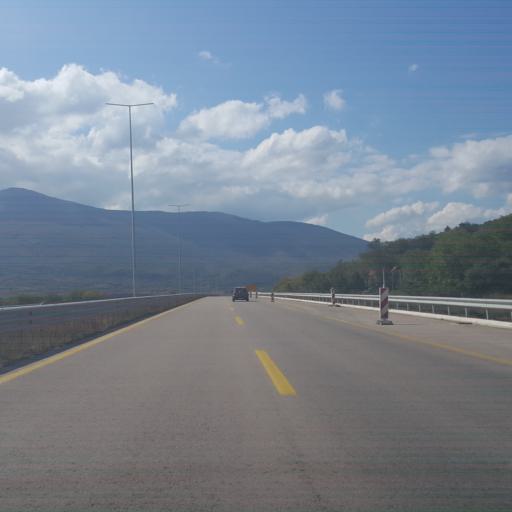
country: RS
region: Central Serbia
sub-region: Pirotski Okrug
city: Bela Palanka
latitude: 43.2360
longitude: 22.3218
